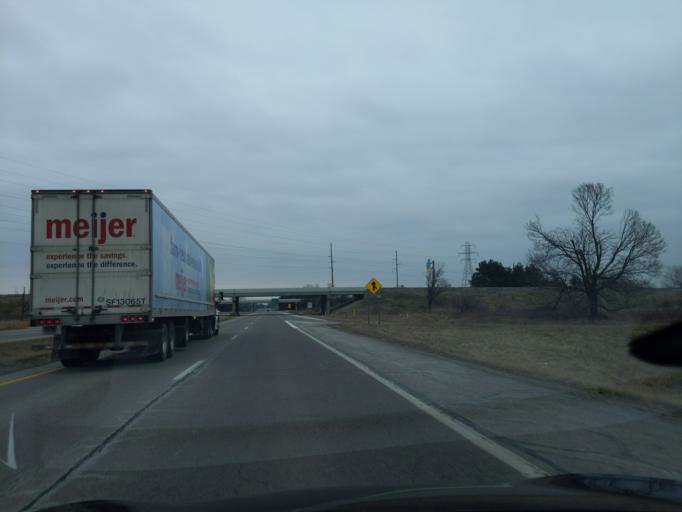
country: US
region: Michigan
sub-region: Eaton County
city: Dimondale
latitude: 42.6752
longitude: -84.6547
